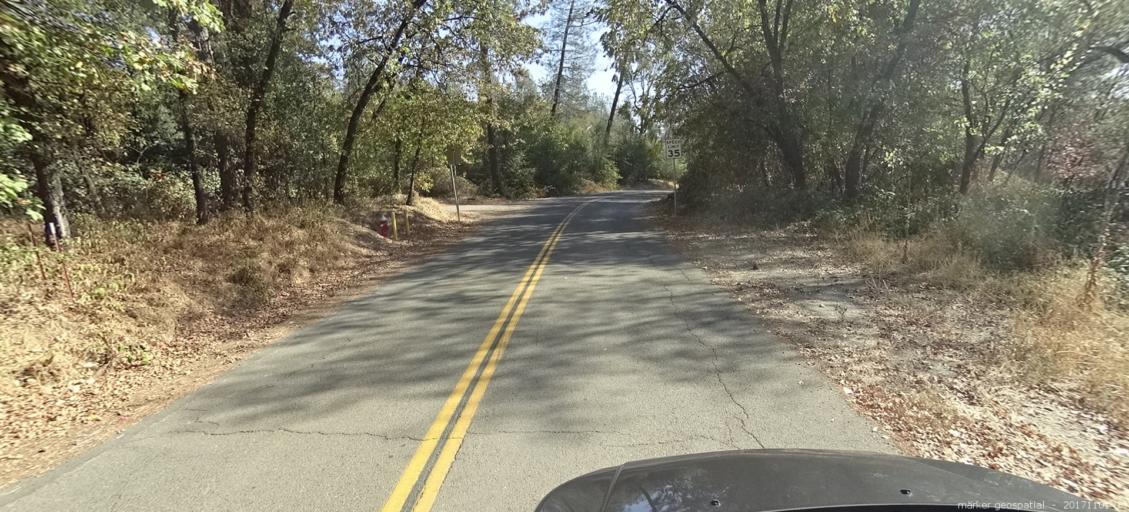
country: US
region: California
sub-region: Shasta County
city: Central Valley (historical)
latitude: 40.6764
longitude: -122.4067
